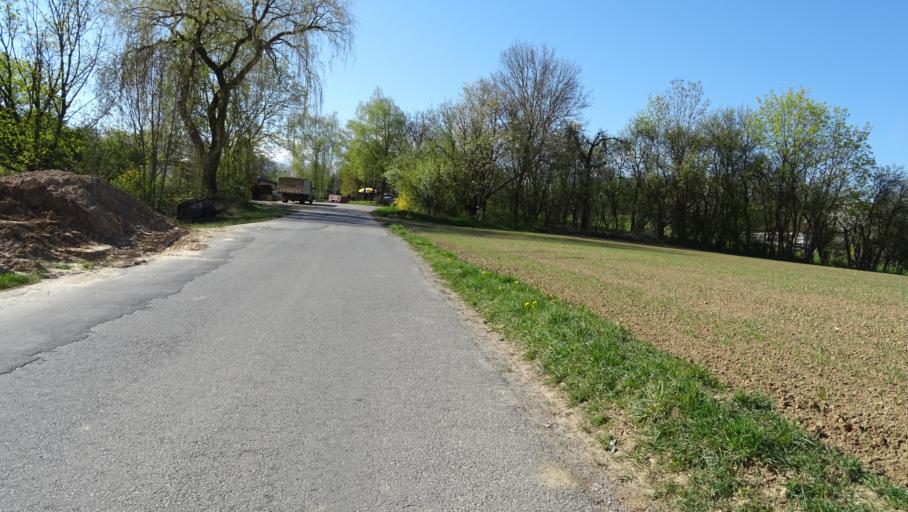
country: DE
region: Baden-Wuerttemberg
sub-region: Karlsruhe Region
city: Billigheim
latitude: 49.3893
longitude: 9.2629
